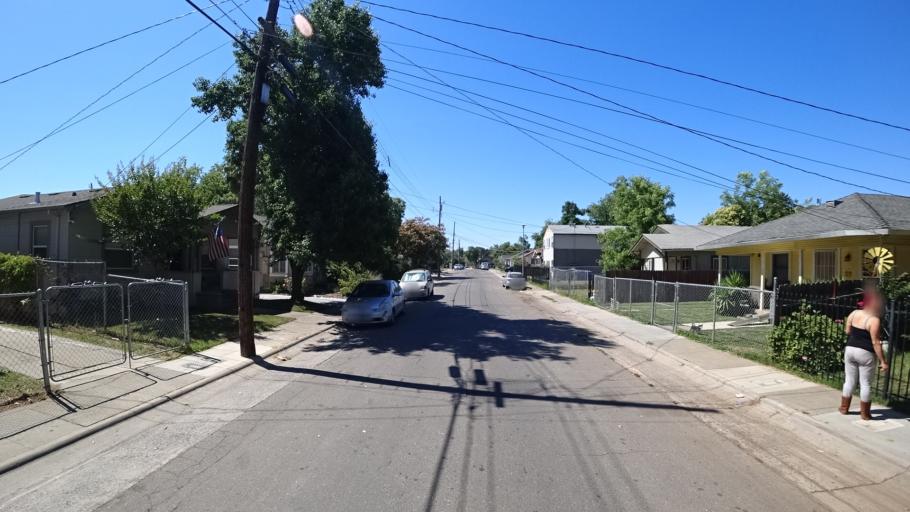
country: US
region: California
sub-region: Sacramento County
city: Parkway
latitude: 38.5459
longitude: -121.4567
